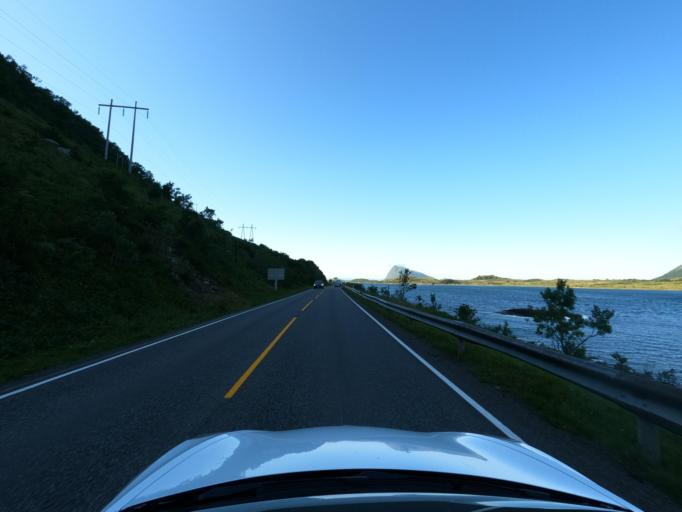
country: NO
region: Nordland
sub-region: Vagan
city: Kabelvag
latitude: 68.2693
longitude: 14.1501
